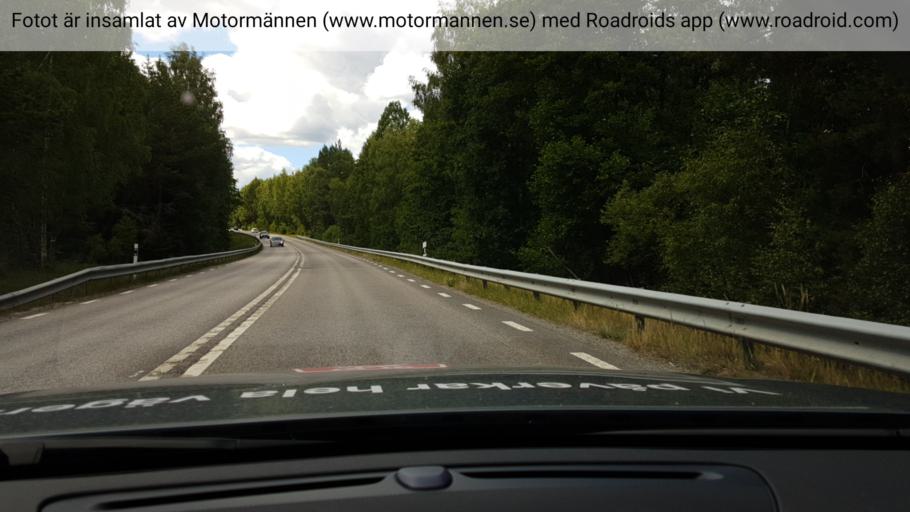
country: SE
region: Stockholm
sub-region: Osterakers Kommun
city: Akersberga
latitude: 59.4282
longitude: 18.2362
